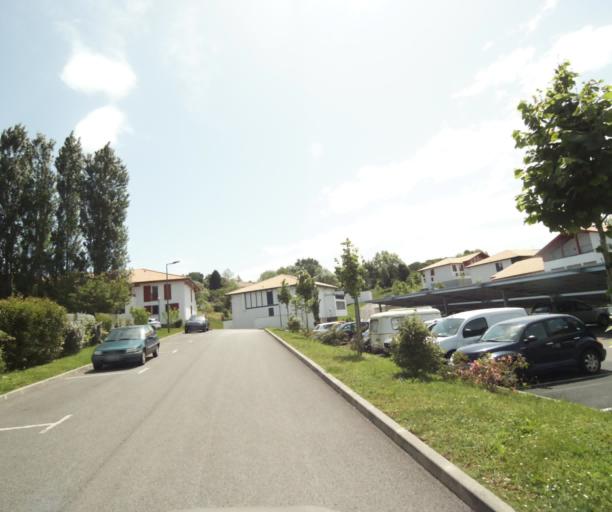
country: FR
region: Aquitaine
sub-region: Departement des Pyrenees-Atlantiques
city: Mouguerre
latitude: 43.4614
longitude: -1.4428
